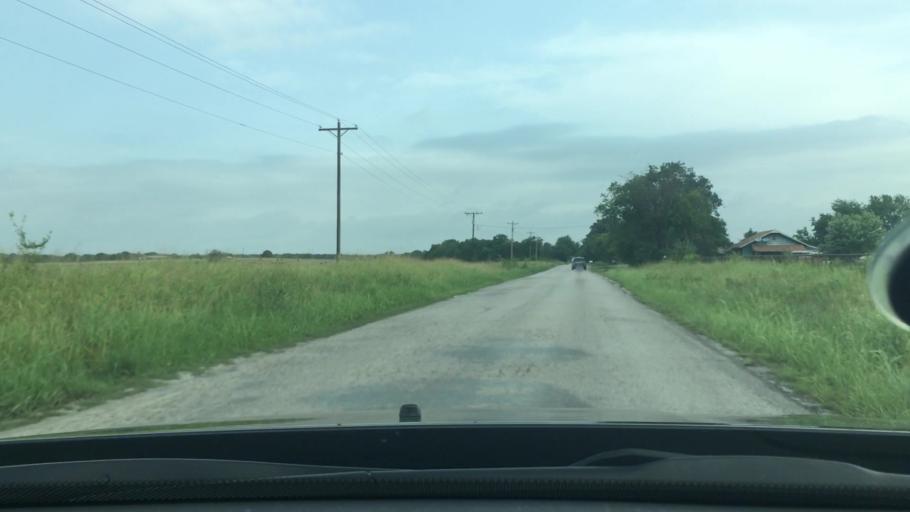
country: US
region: Oklahoma
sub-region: Carter County
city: Lone Grove
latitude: 34.2082
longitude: -97.2650
